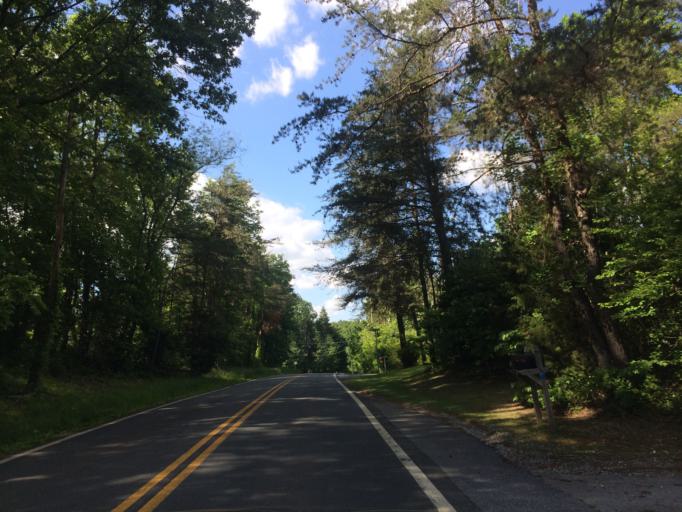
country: US
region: Maryland
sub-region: Carroll County
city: Eldersburg
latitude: 39.4415
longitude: -76.9935
